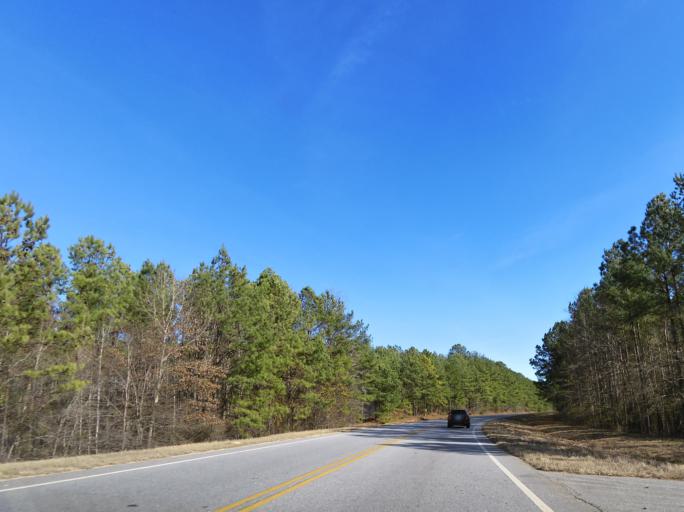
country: US
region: Georgia
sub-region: Crawford County
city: Roberta
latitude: 32.7504
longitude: -84.0823
